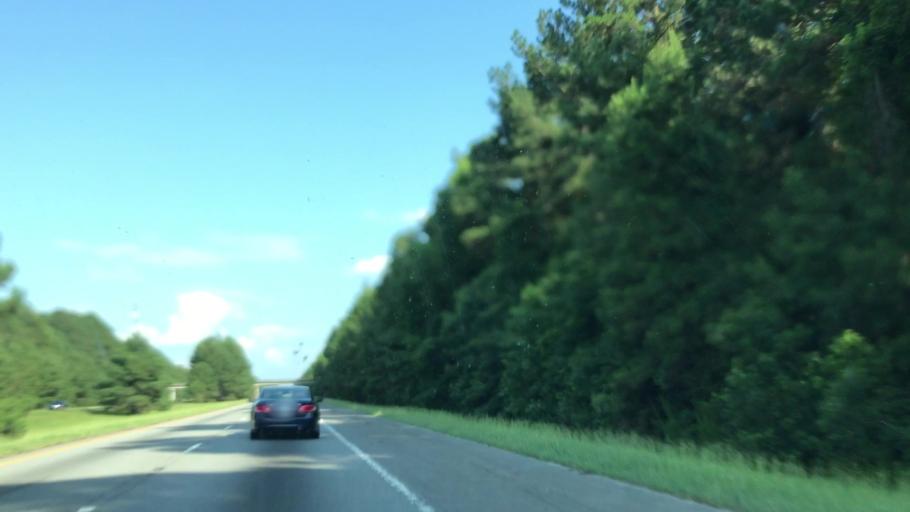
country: US
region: South Carolina
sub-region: Orangeburg County
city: Brookdale
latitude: 33.4286
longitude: -80.6895
